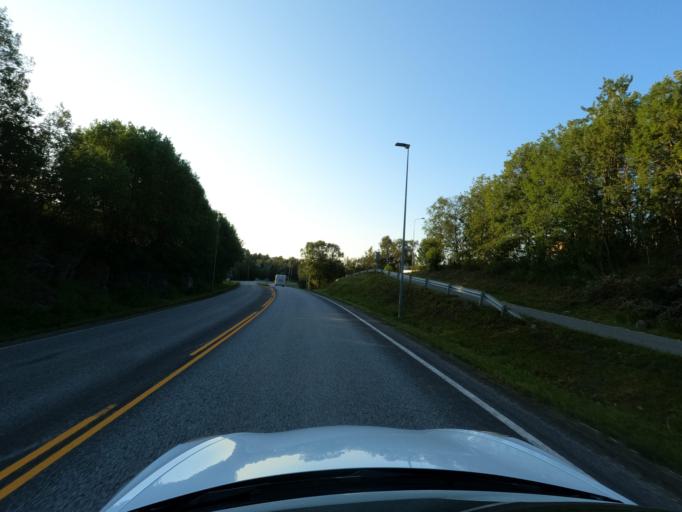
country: NO
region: Troms
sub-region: Harstad
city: Harstad
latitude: 68.7530
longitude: 16.5673
